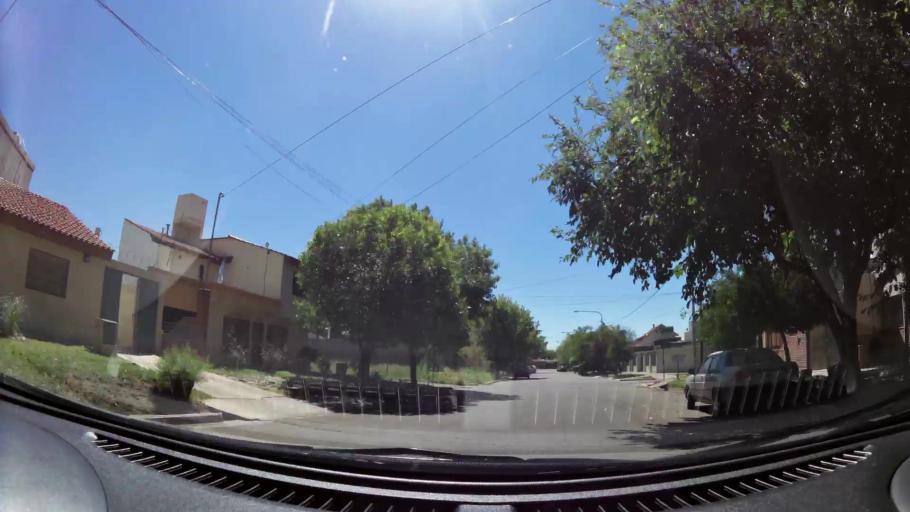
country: AR
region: Mendoza
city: Las Heras
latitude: -32.8541
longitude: -68.8504
